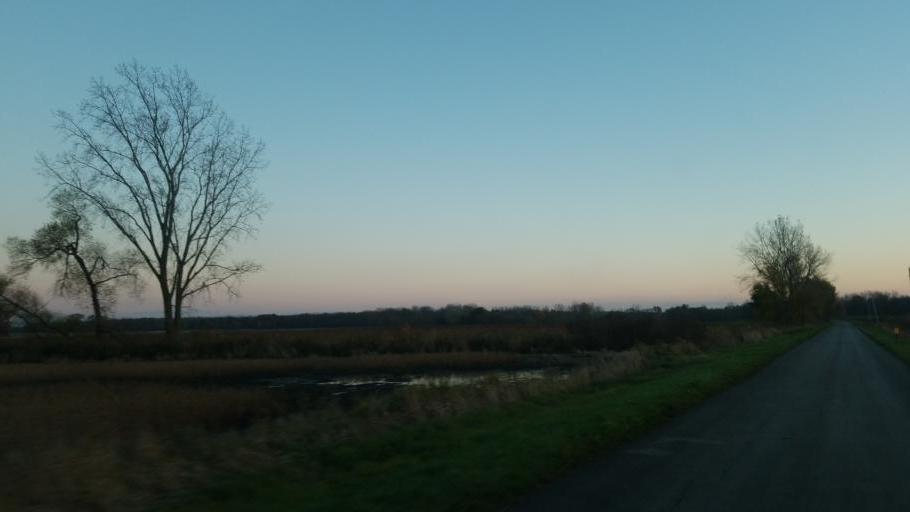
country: US
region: Ohio
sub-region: Huron County
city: Willard
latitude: 41.0303
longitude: -82.7819
